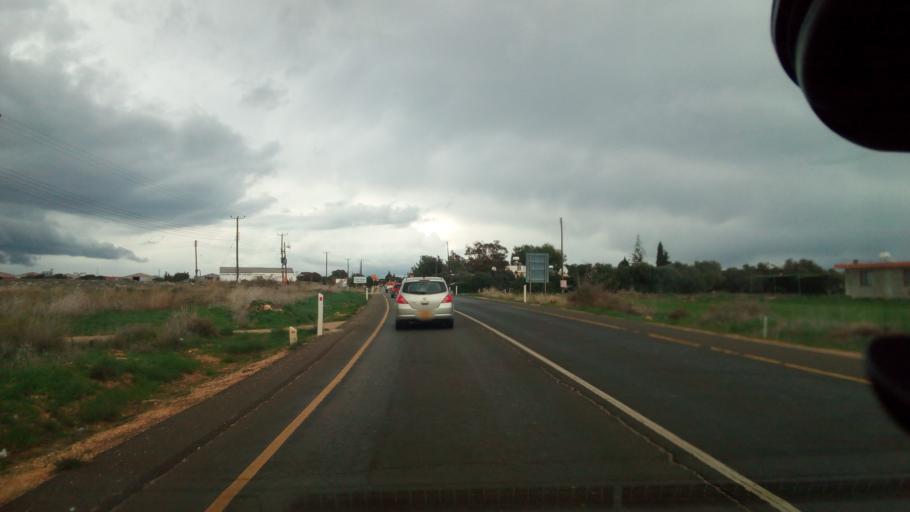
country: CY
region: Ammochostos
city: Frenaros
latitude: 35.0282
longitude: 33.9124
